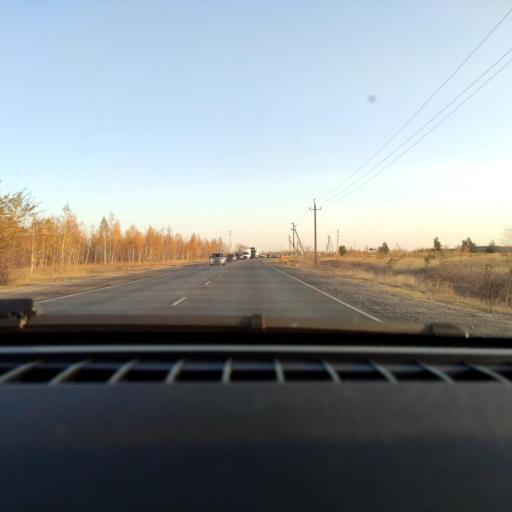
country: RU
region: Voronezj
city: Maslovka
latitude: 51.5795
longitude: 39.2640
